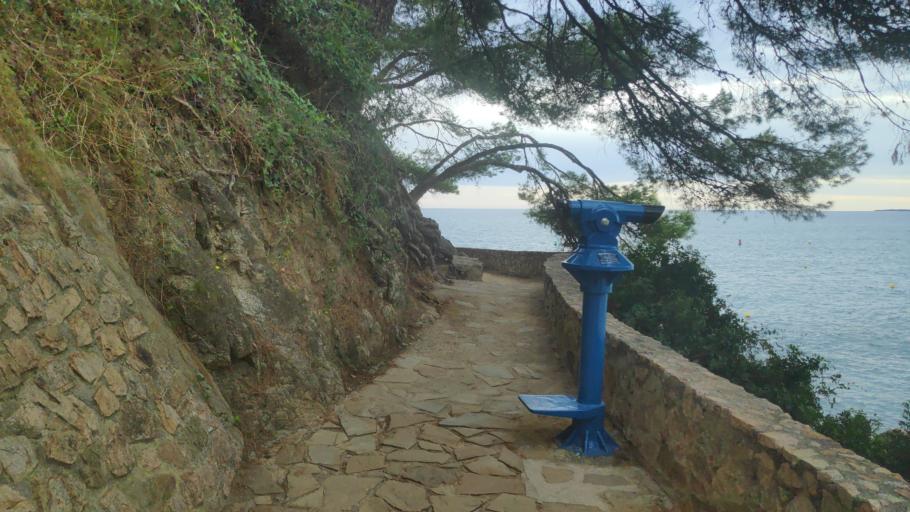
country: ES
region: Catalonia
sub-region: Provincia de Girona
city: Lloret de Mar
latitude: 41.6996
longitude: 2.8594
